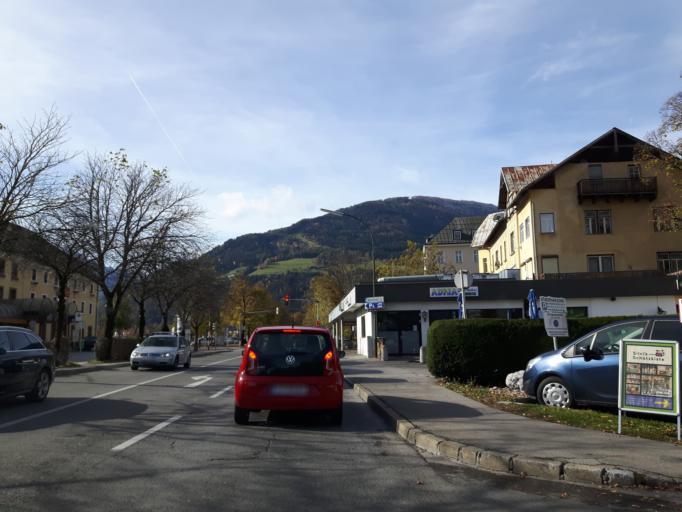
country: AT
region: Tyrol
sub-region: Politischer Bezirk Lienz
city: Lienz
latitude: 46.8278
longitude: 12.7635
